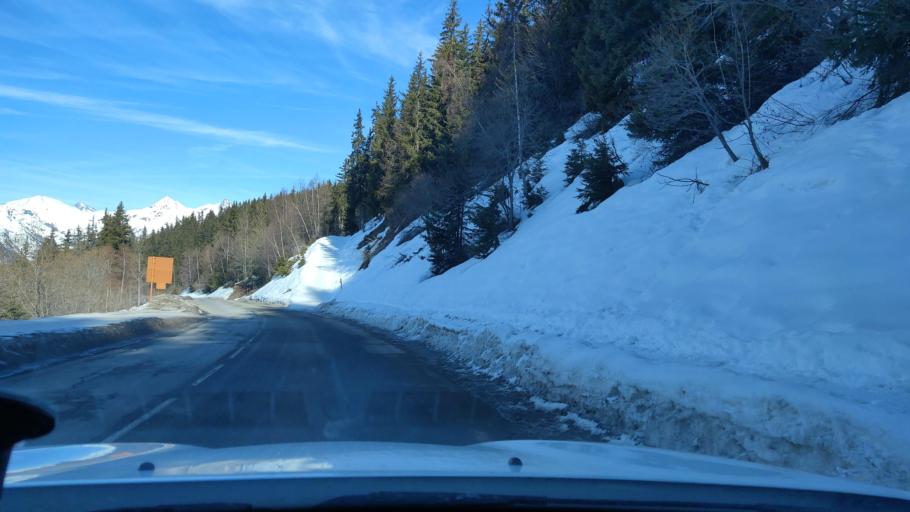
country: FR
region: Rhone-Alpes
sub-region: Departement de la Savoie
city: Bourg-Saint-Maurice
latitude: 45.5801
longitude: 6.7884
